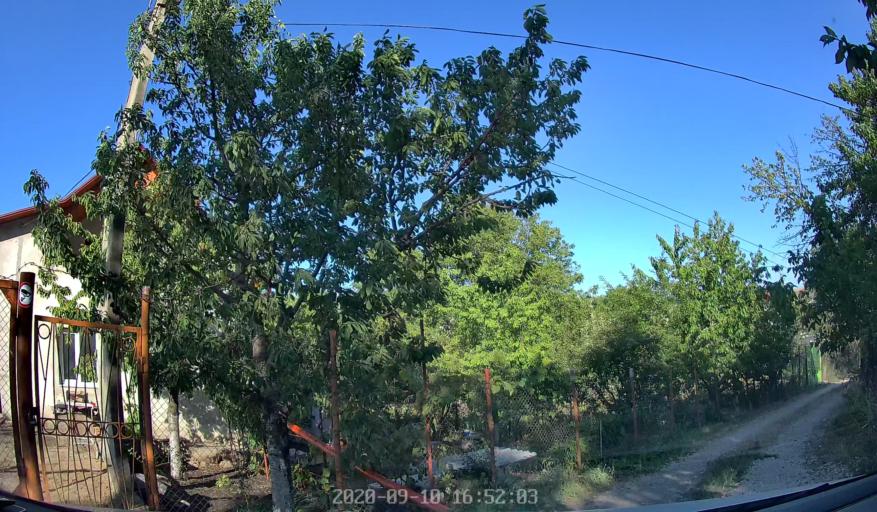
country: MD
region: Chisinau
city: Stauceni
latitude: 47.0574
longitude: 28.9222
